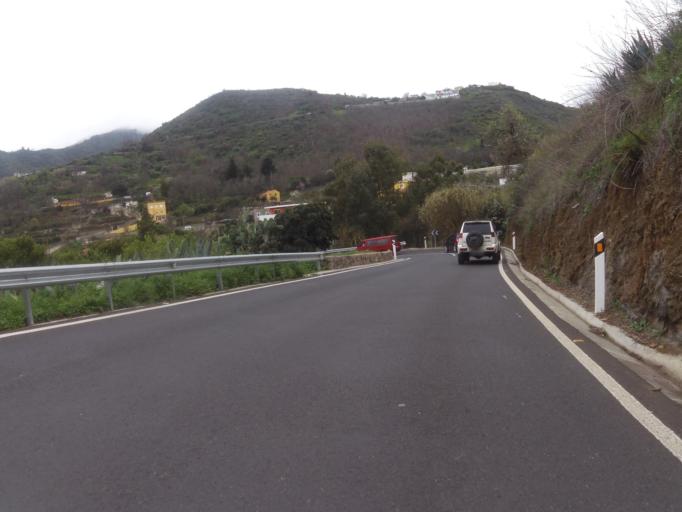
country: ES
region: Canary Islands
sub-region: Provincia de Las Palmas
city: Vega de San Mateo
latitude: 28.0076
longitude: -15.5431
